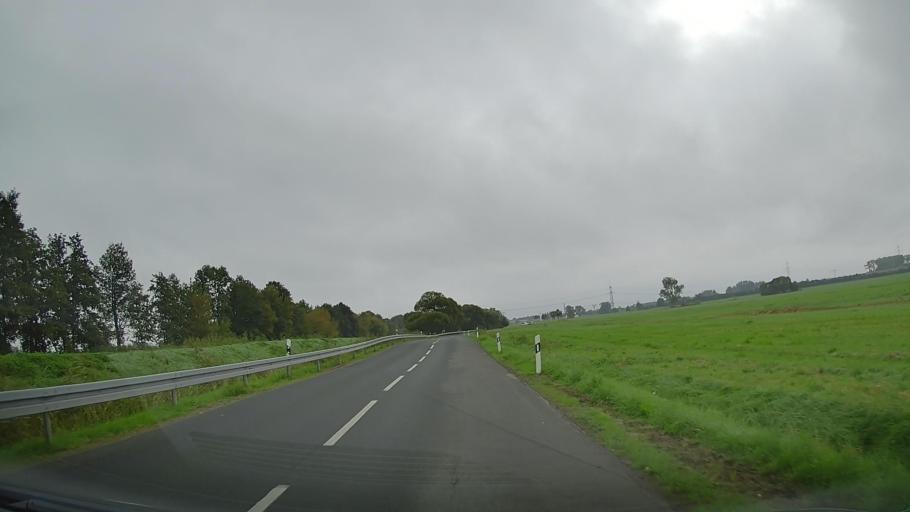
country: DE
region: Mecklenburg-Vorpommern
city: Guestrow
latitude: 53.8151
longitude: 12.1335
